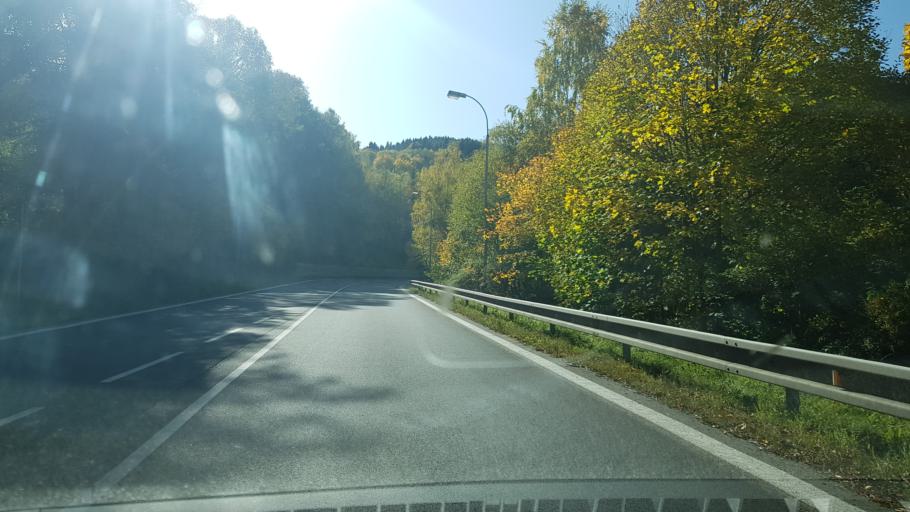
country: CZ
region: Jihocesky
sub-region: Okres Prachatice
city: Vimperk
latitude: 49.0523
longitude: 13.7780
